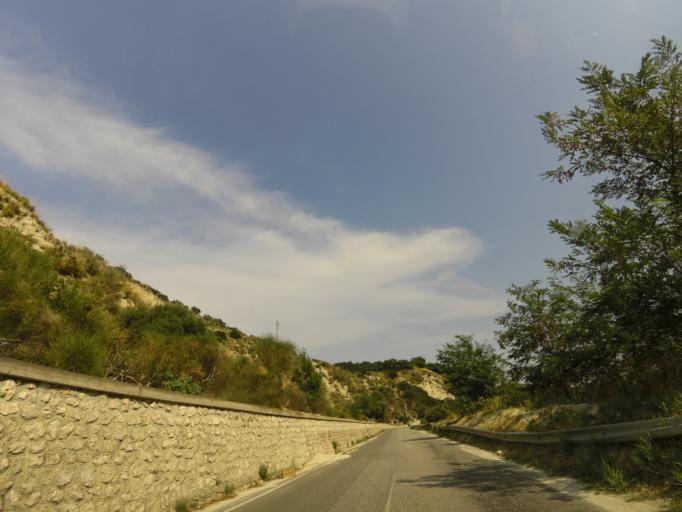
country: IT
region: Calabria
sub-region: Provincia di Reggio Calabria
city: Monasterace
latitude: 38.4624
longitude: 16.5175
